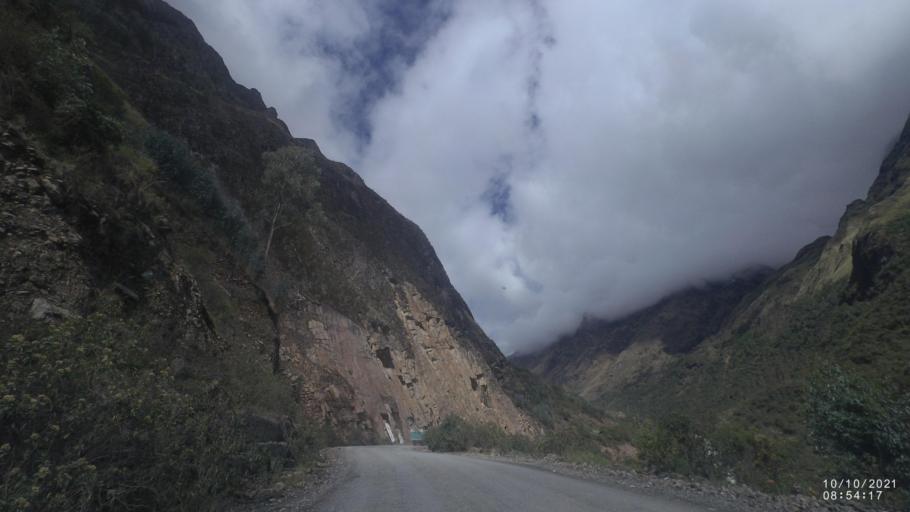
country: BO
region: La Paz
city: Quime
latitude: -16.9886
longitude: -67.2335
